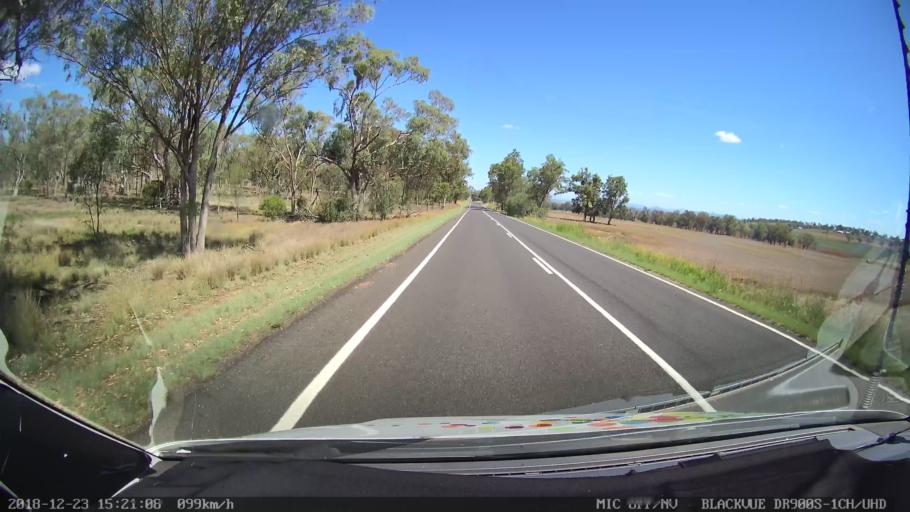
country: AU
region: New South Wales
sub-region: Tamworth Municipality
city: Manilla
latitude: -30.8522
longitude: 150.7945
